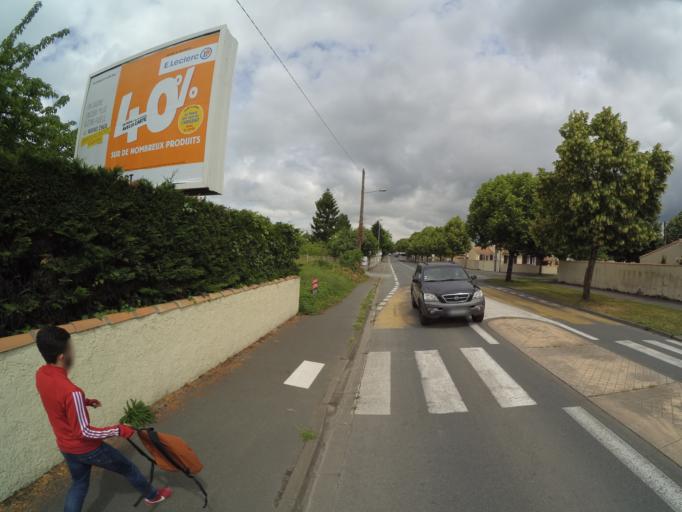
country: FR
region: Poitou-Charentes
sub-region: Departement de la Charente-Maritime
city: Rochefort
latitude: 45.9557
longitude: -0.9692
